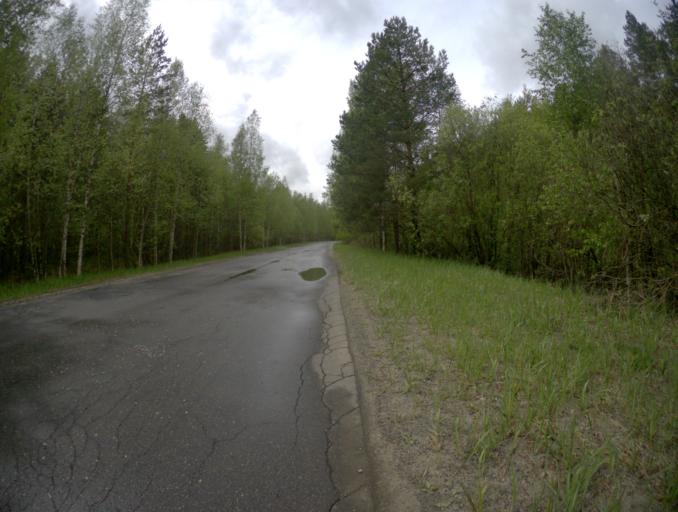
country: RU
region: Vladimir
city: Zolotkovo
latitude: 55.3471
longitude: 40.9558
